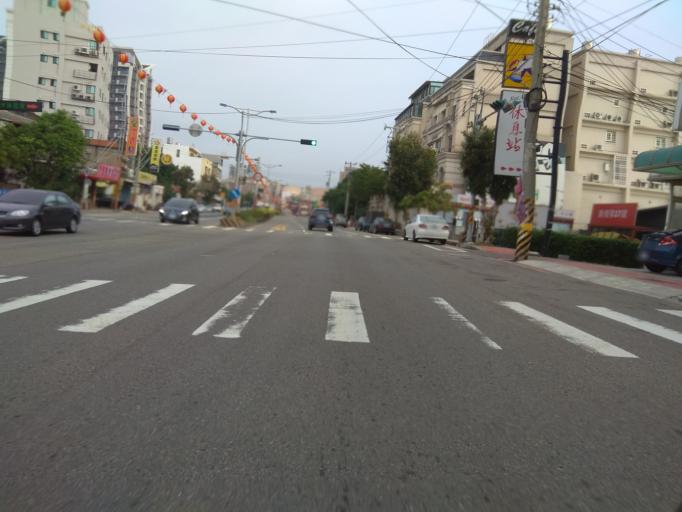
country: TW
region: Taiwan
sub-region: Hsinchu
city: Hsinchu
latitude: 24.8363
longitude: 120.9296
